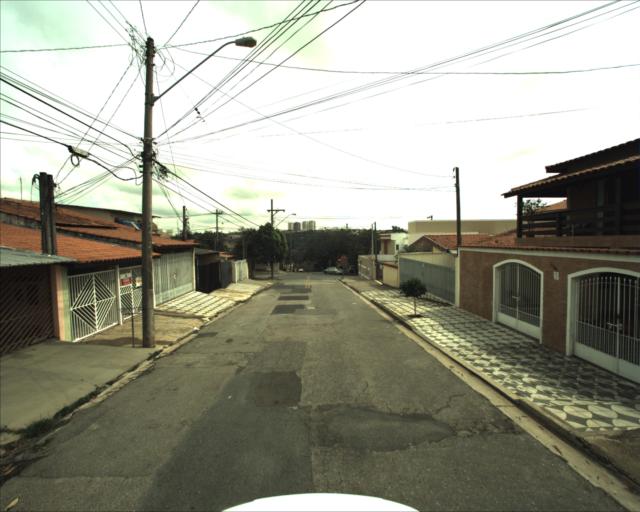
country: BR
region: Sao Paulo
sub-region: Sorocaba
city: Sorocaba
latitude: -23.4999
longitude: -47.4958
